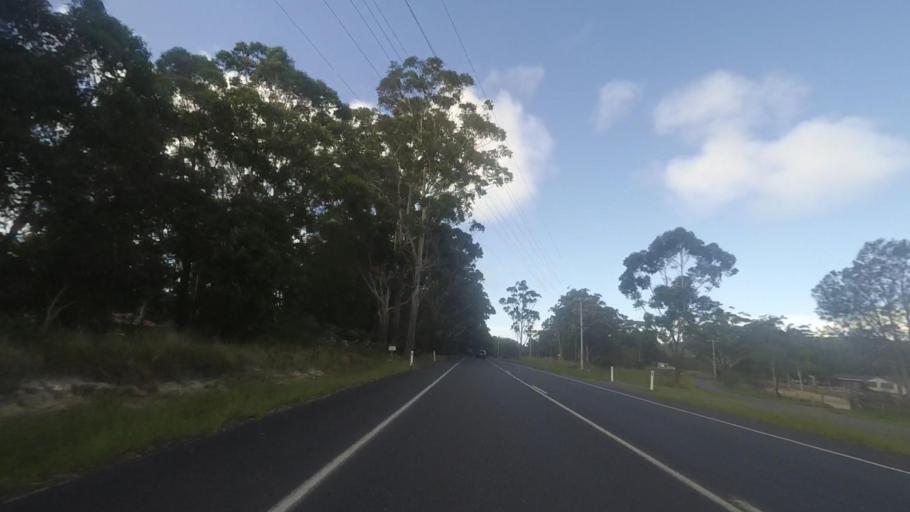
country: AU
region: New South Wales
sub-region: Great Lakes
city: Forster
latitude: -32.3574
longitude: 152.5044
